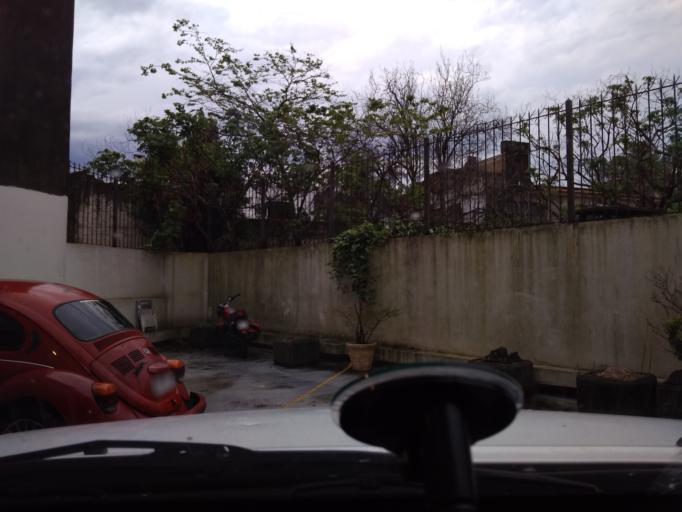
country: UY
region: Canelones
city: Paso de Carrasco
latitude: -34.8956
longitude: -56.1108
